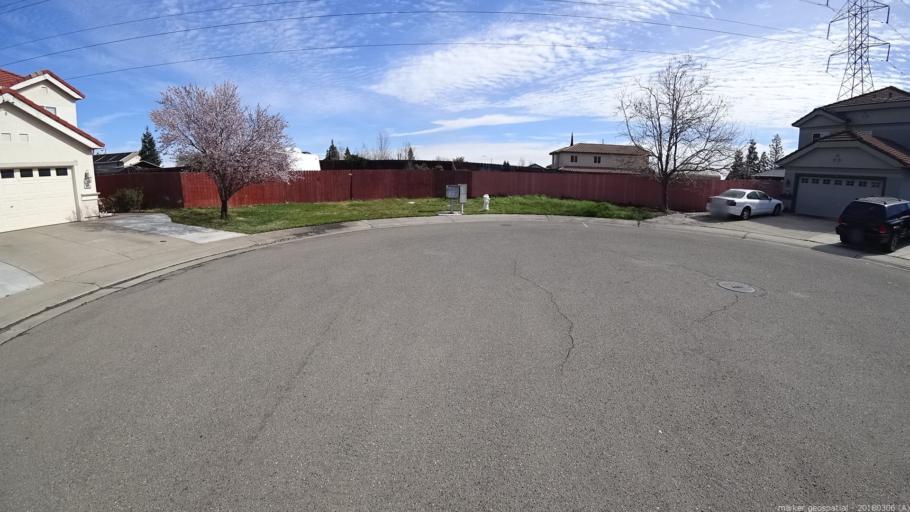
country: US
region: California
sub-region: Sacramento County
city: Vineyard
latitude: 38.4636
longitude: -121.3456
